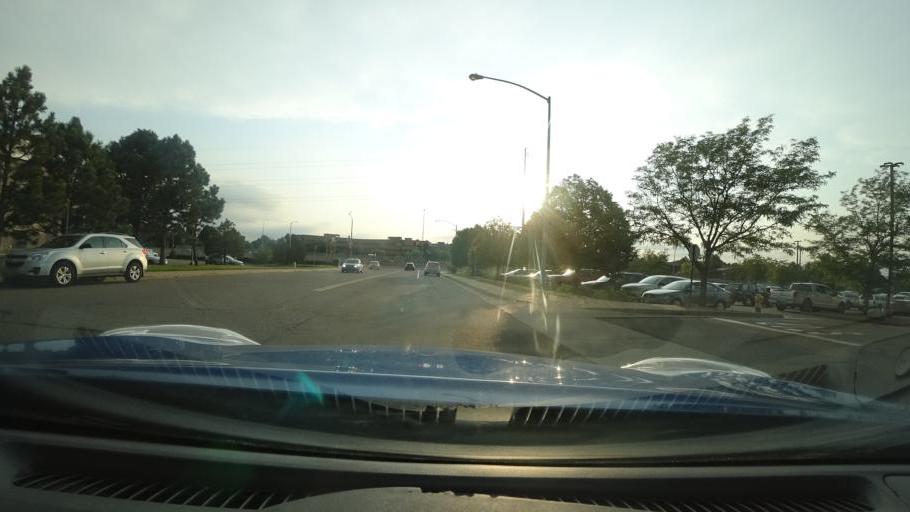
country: US
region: Colorado
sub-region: Adams County
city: Aurora
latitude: 39.6894
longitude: -104.8272
